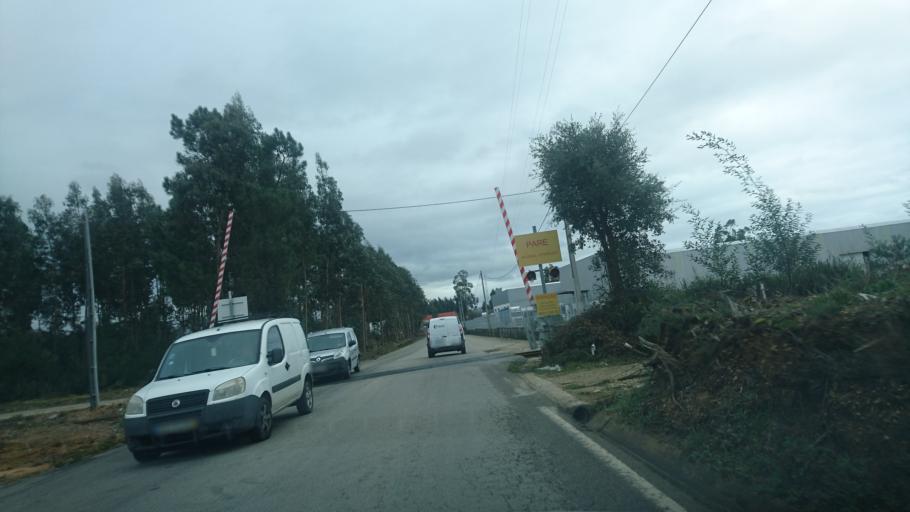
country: PT
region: Aveiro
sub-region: Agueda
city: Agueda
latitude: 40.5953
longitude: -8.4545
